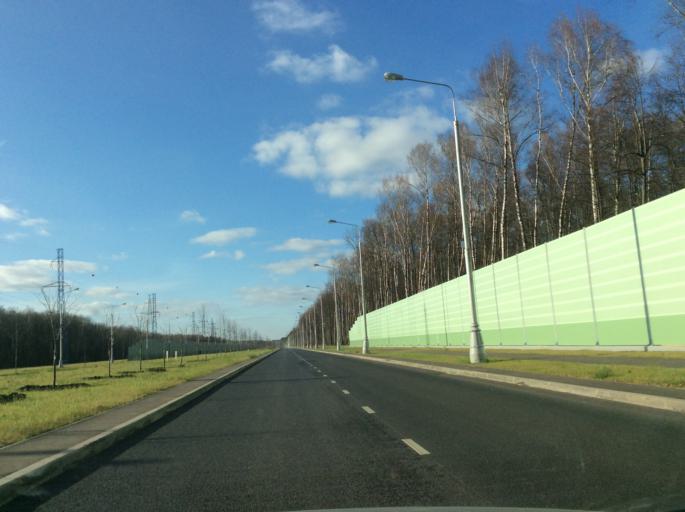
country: RU
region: Moskovskaya
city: Vatutinki
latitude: 55.4826
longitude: 37.3677
